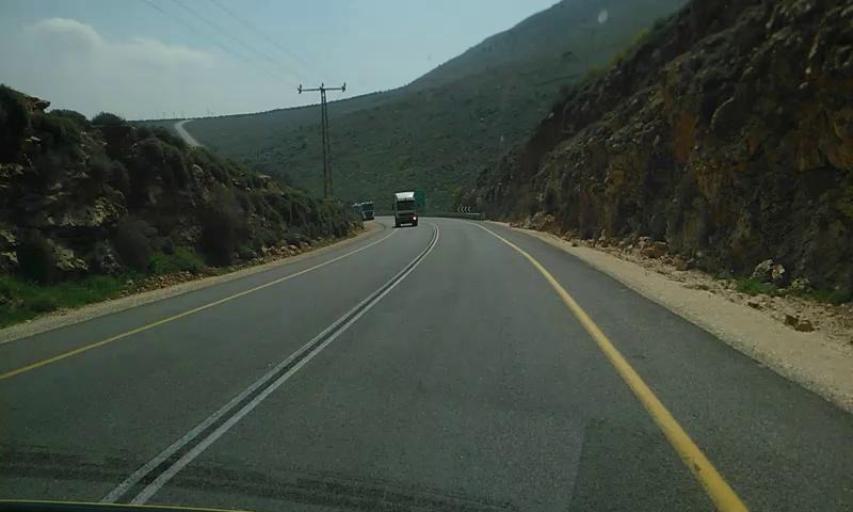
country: PS
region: West Bank
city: Majdal Bani Fadil
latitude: 32.0761
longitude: 35.3523
